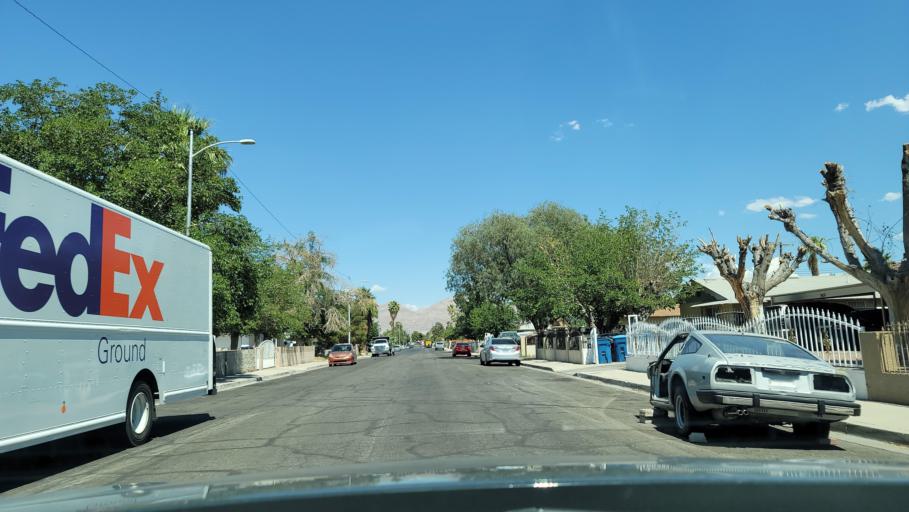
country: US
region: Nevada
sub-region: Clark County
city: North Las Vegas
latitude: 36.1838
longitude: -115.1227
